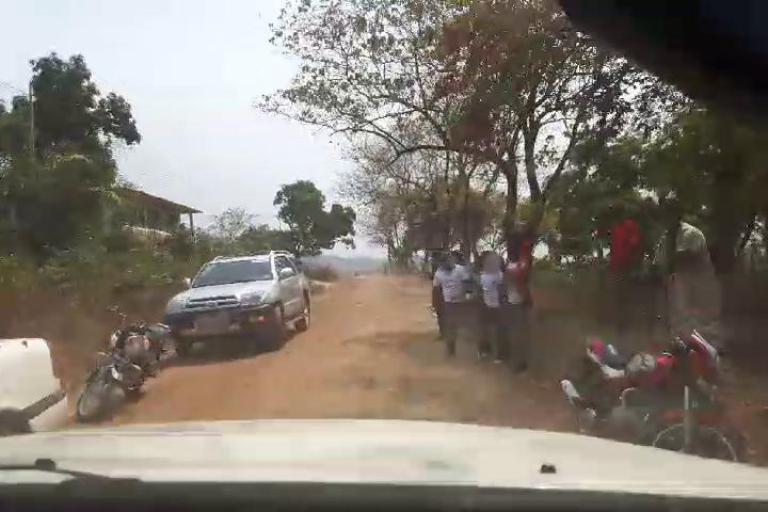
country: SL
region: Northern Province
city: Bumbuna
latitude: 9.0376
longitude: -11.7591
